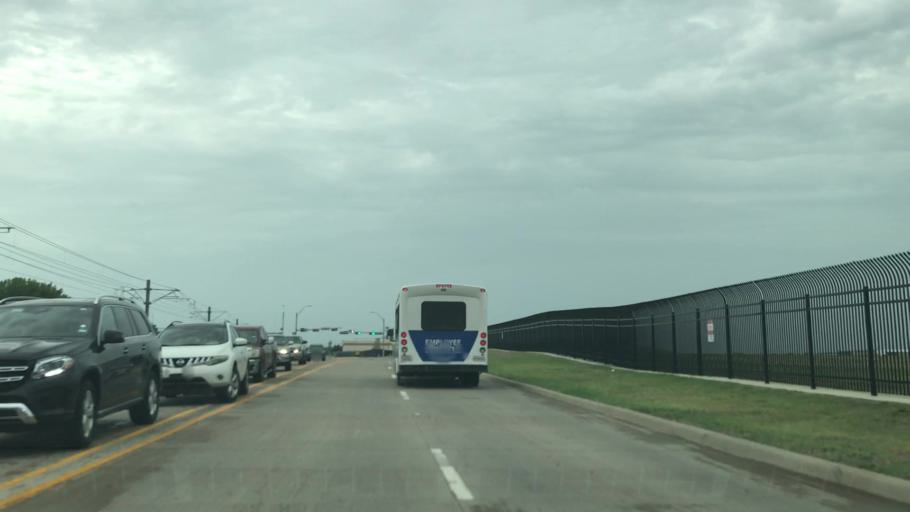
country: US
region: Texas
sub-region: Dallas County
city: University Park
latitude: 32.8382
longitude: -96.8512
